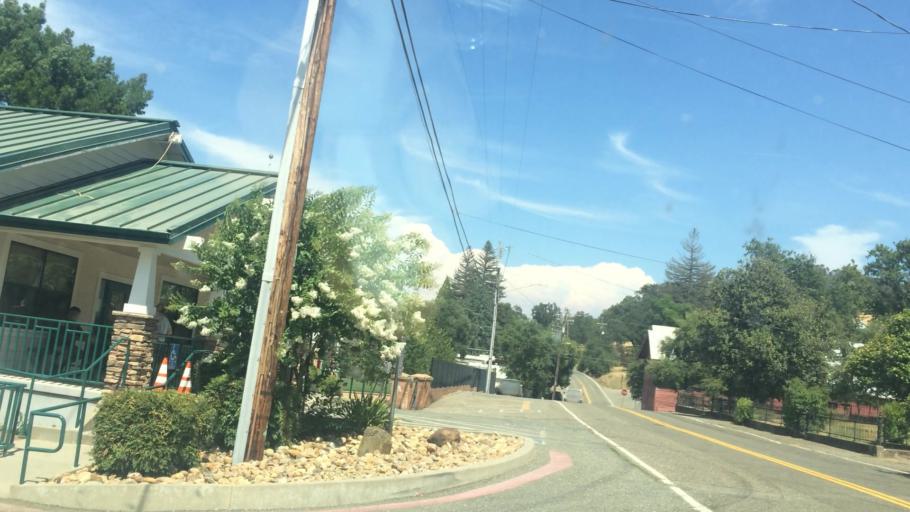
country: US
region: California
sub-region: Amador County
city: Sutter Creek
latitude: 38.3919
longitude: -120.8017
